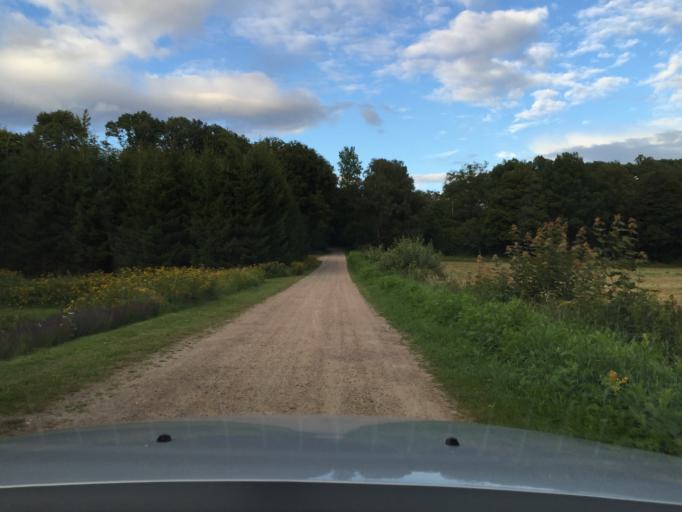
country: SE
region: Skane
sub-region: Hassleholms Kommun
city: Sosdala
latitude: 56.0448
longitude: 13.7100
